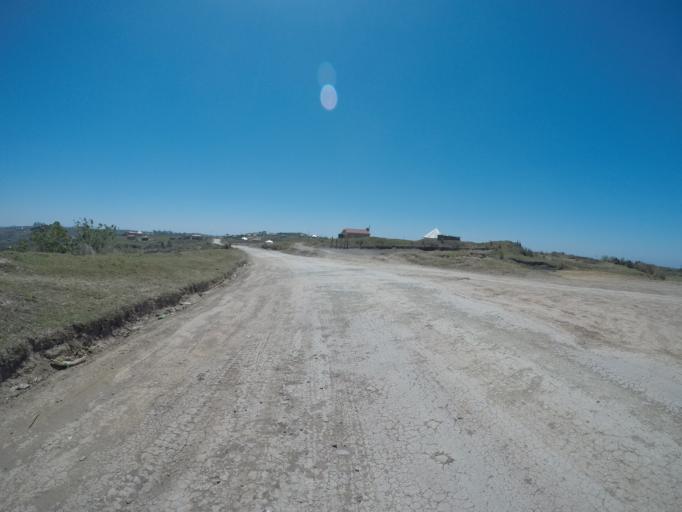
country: ZA
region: Eastern Cape
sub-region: OR Tambo District Municipality
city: Libode
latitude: -31.9442
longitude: 29.0273
